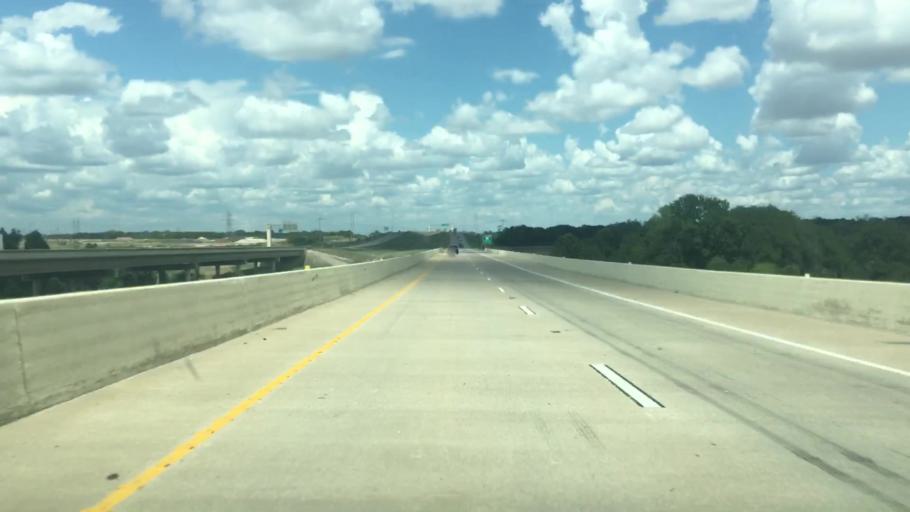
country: US
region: Texas
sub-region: Williamson County
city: Georgetown
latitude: 30.6537
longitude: -97.6358
